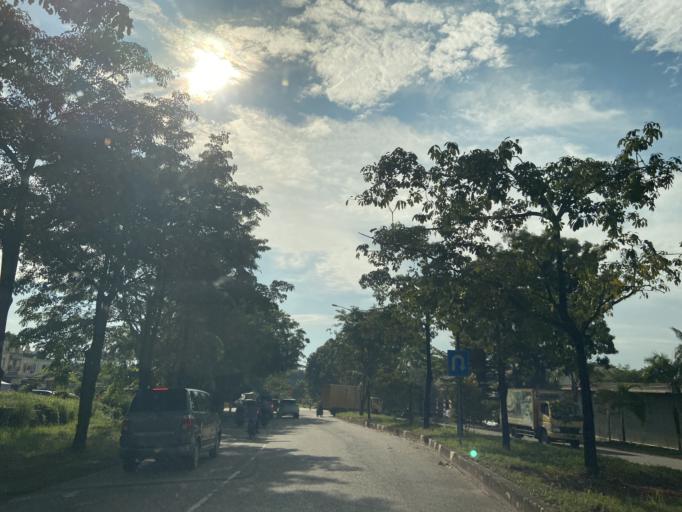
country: SG
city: Singapore
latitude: 1.1078
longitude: 104.0640
